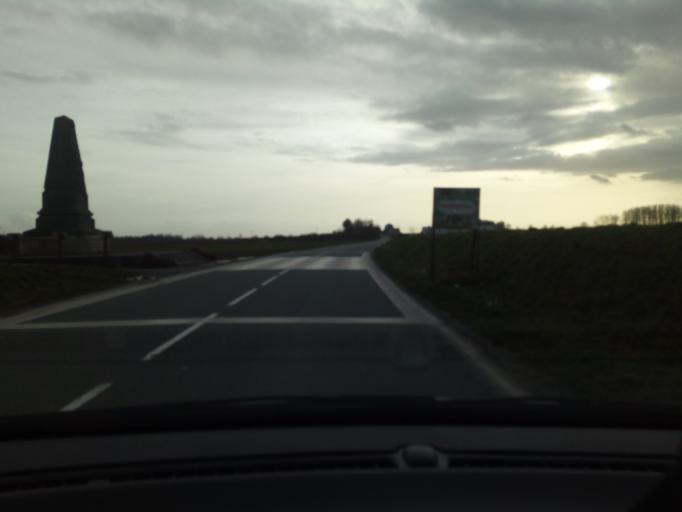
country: FR
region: Nord-Pas-de-Calais
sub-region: Departement du Nord
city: La Longueville
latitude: 50.3338
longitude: 3.8714
